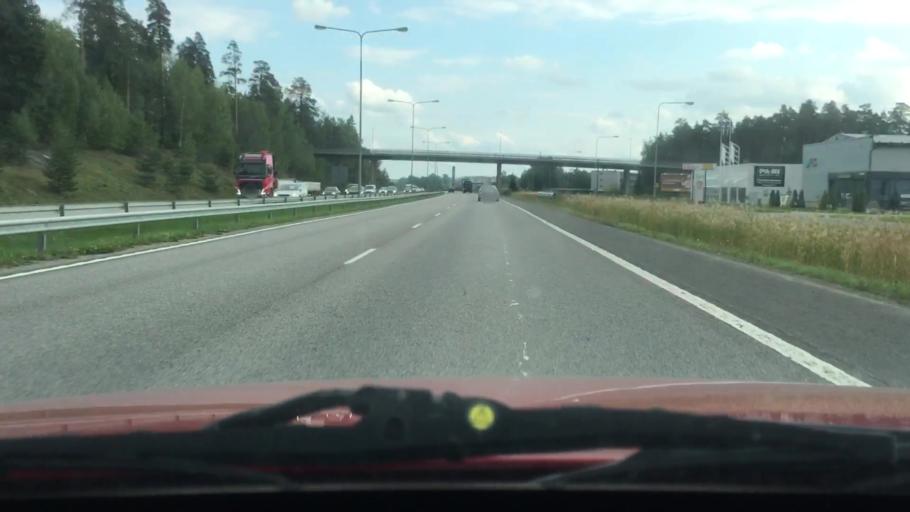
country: FI
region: Varsinais-Suomi
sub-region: Turku
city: Raisio
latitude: 60.4975
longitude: 22.1636
